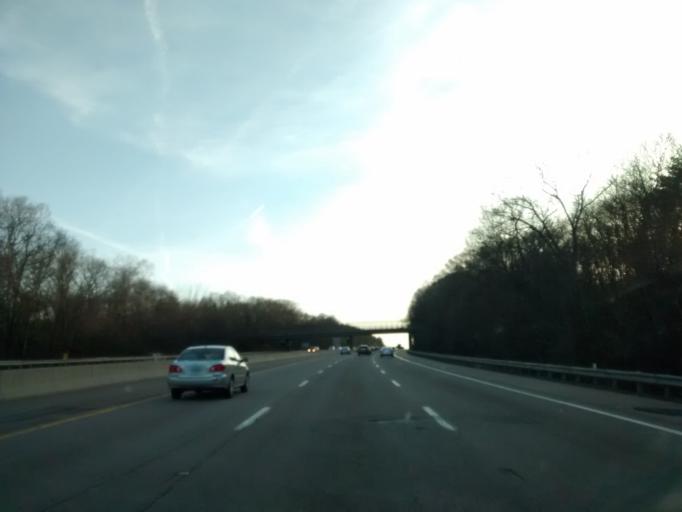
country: US
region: Massachusetts
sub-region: Worcester County
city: Cordaville
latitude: 42.2862
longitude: -71.4959
